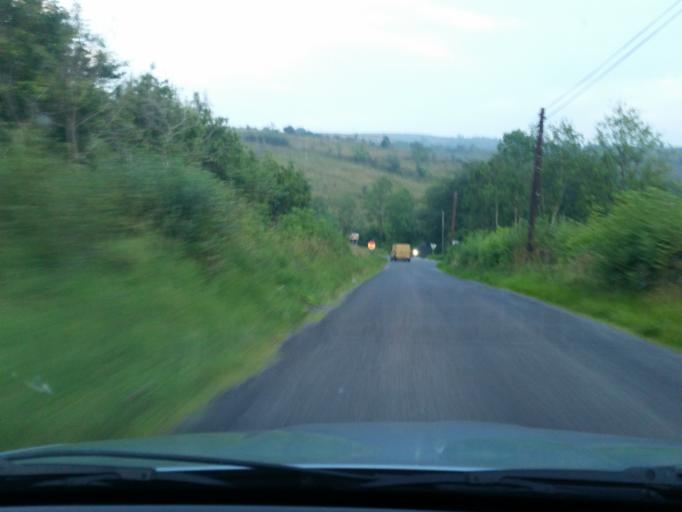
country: GB
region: Northern Ireland
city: Fivemiletown
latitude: 54.2920
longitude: -7.2803
